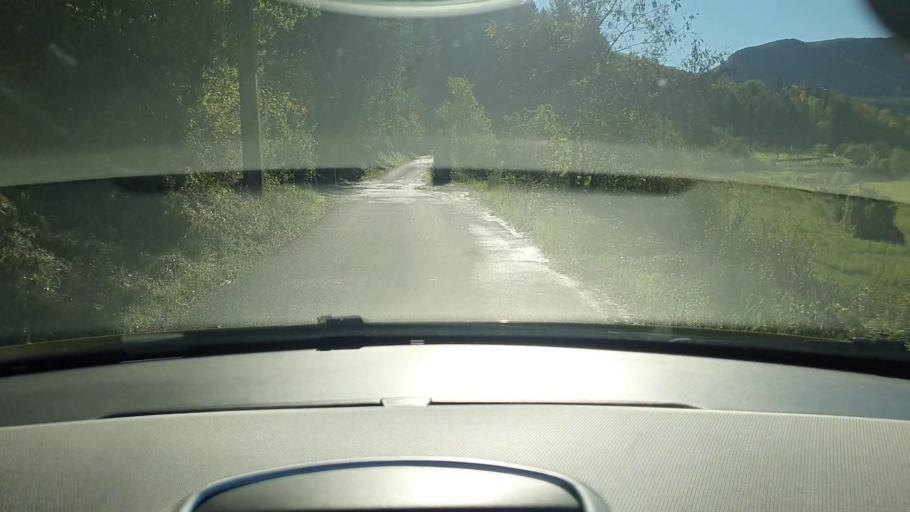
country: FR
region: Languedoc-Roussillon
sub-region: Departement du Gard
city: Le Vigan
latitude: 43.9857
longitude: 3.6090
